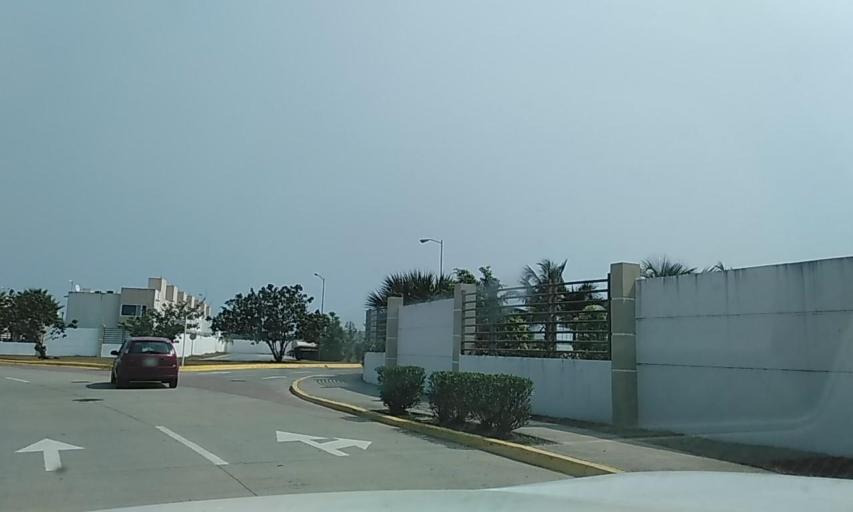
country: MX
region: Veracruz
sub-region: Veracruz
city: Hacienda Sotavento
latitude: 19.1322
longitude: -96.1673
